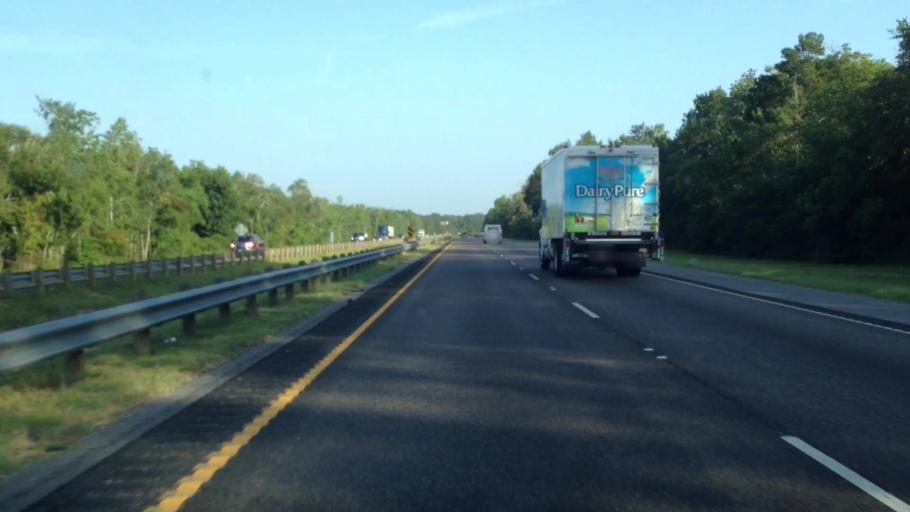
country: US
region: Louisiana
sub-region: Tangipahoa Parish
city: Ponchatoula
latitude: 30.4172
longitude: -90.4407
